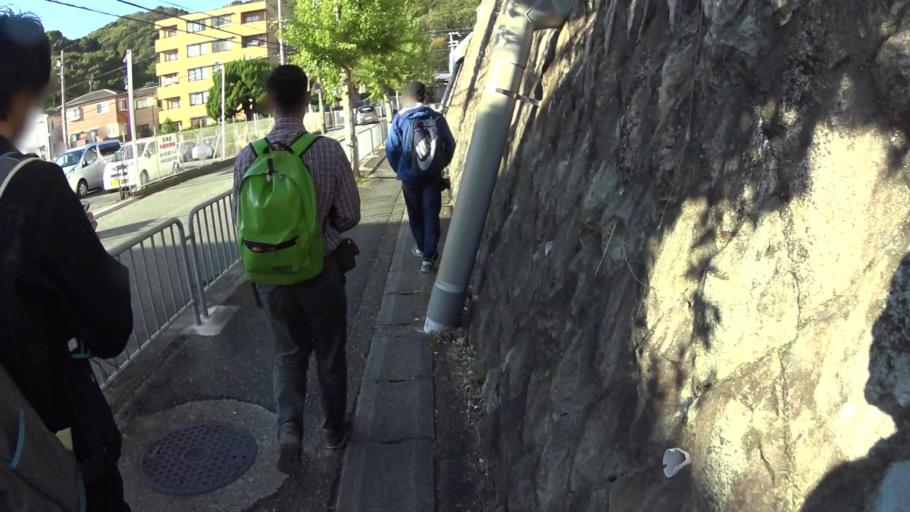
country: JP
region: Osaka
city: Ikeda
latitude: 34.8282
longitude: 135.4323
